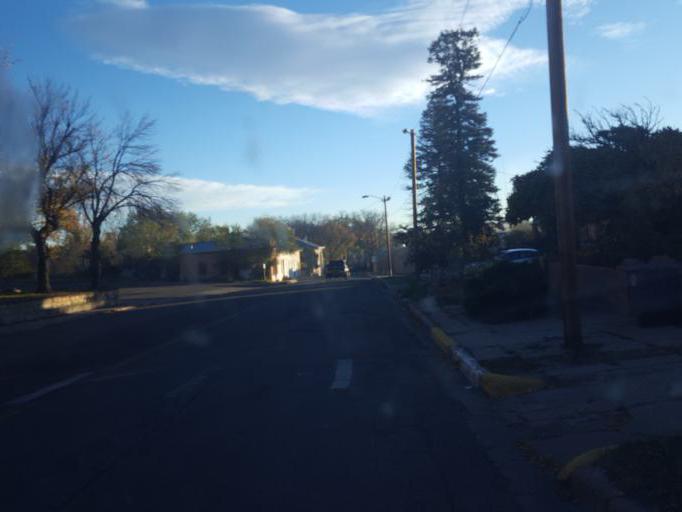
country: US
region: New Mexico
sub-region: San Miguel County
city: Las Vegas
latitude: 35.5916
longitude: -105.2292
